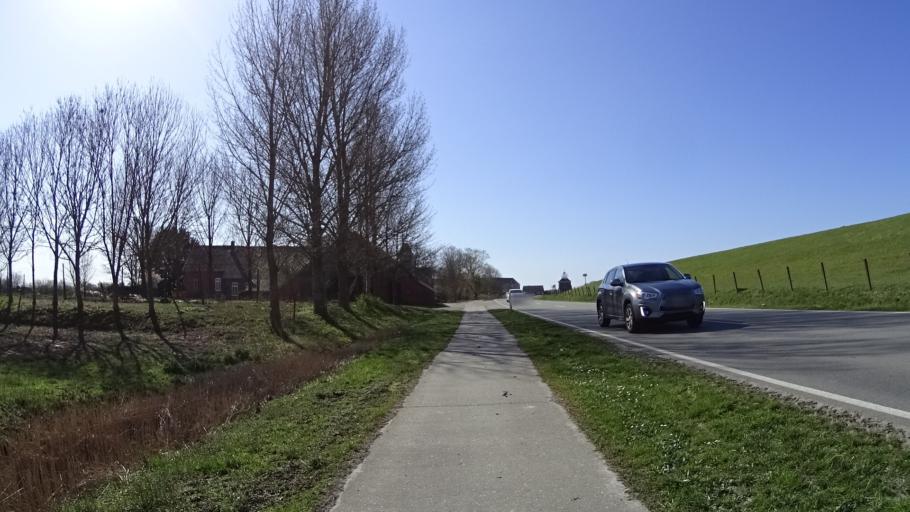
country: DE
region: Lower Saxony
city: Jemgum
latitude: 53.2569
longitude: 7.4061
